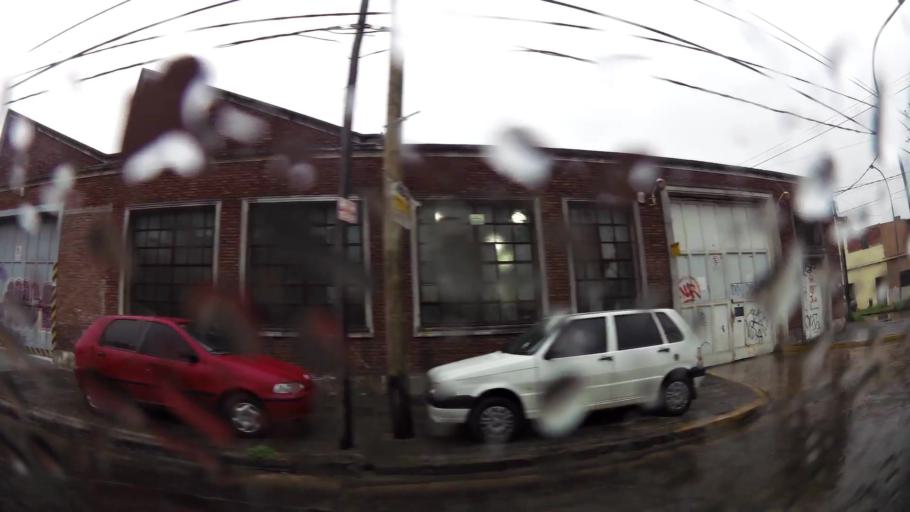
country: AR
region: Buenos Aires
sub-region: Partido de Lanus
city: Lanus
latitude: -34.7099
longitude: -58.4063
